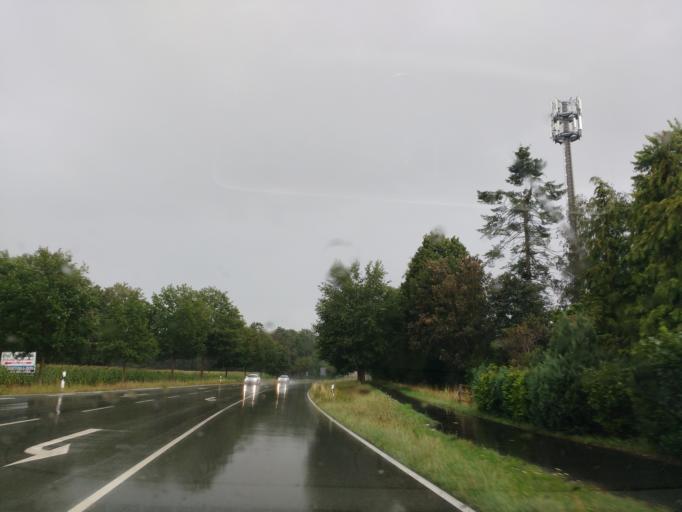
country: DE
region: North Rhine-Westphalia
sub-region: Regierungsbezirk Munster
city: Ladbergen
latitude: 52.1331
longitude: 7.7942
